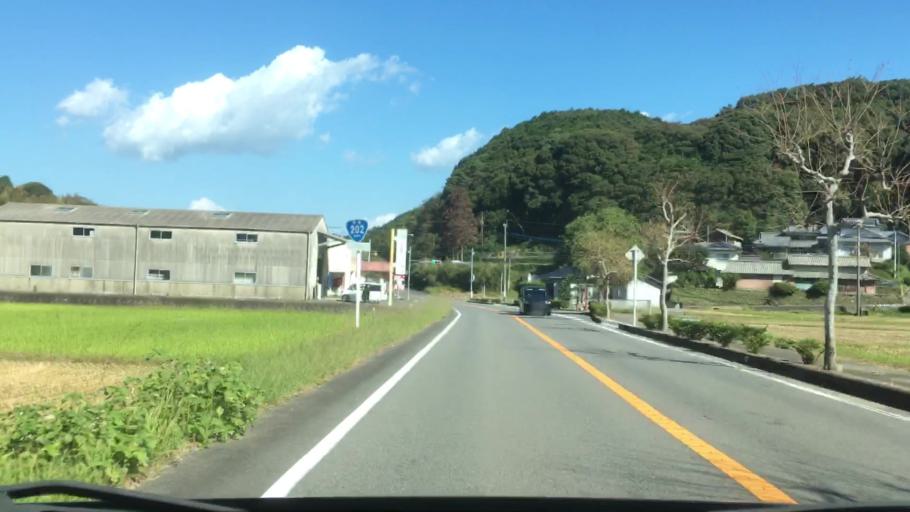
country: JP
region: Nagasaki
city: Sasebo
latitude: 32.9656
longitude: 129.6460
